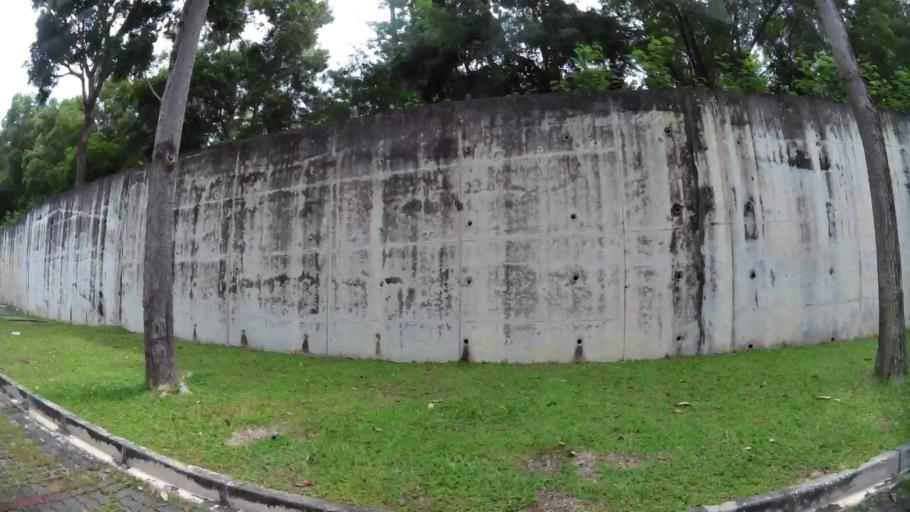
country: SG
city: Singapore
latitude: 1.3523
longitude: 103.9752
